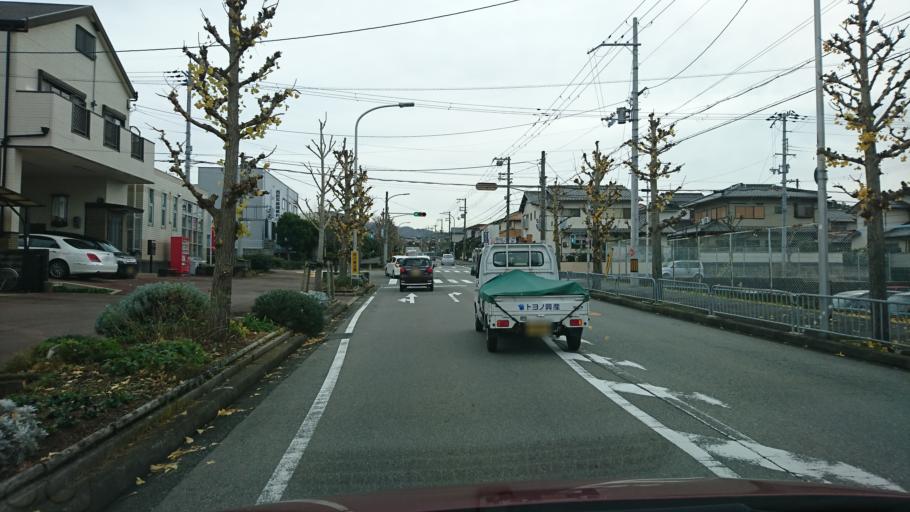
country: JP
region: Osaka
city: Mino
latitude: 34.9013
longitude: 135.4452
